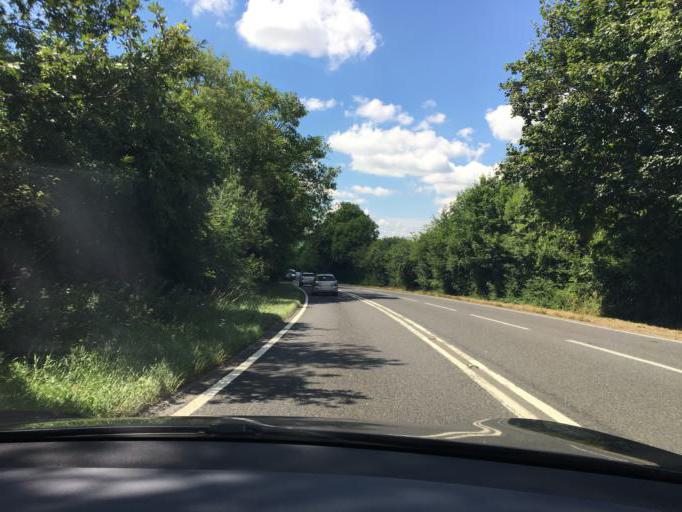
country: GB
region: England
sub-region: Surrey
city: Leatherhead
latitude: 51.2859
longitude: -0.3142
